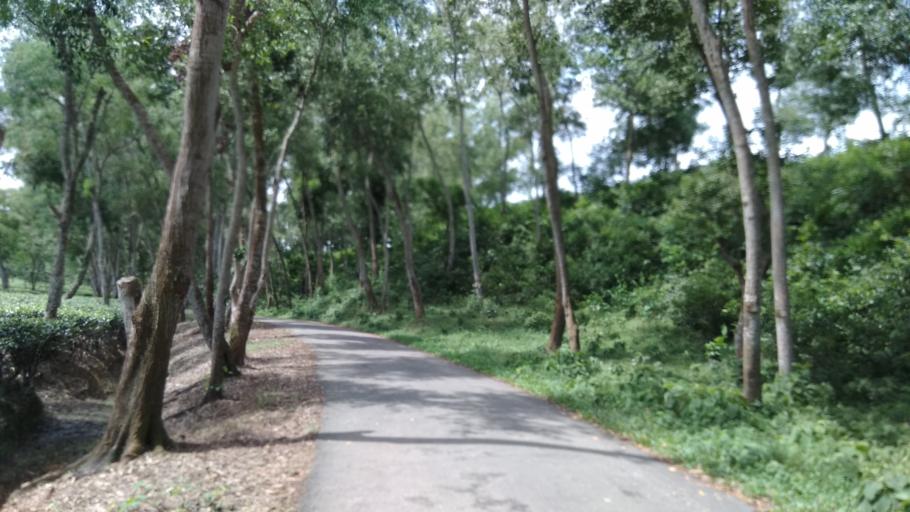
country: IN
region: Tripura
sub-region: Dhalai
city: Kamalpur
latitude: 24.3017
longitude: 91.8213
